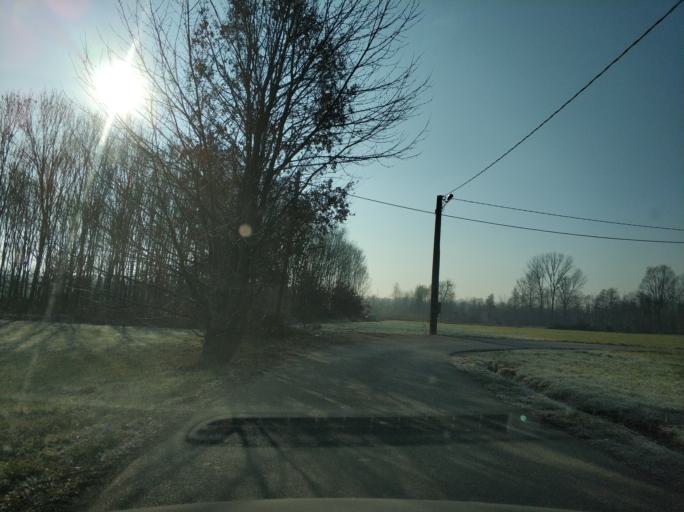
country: IT
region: Piedmont
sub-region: Provincia di Torino
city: Barbania
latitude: 45.3079
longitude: 7.6341
